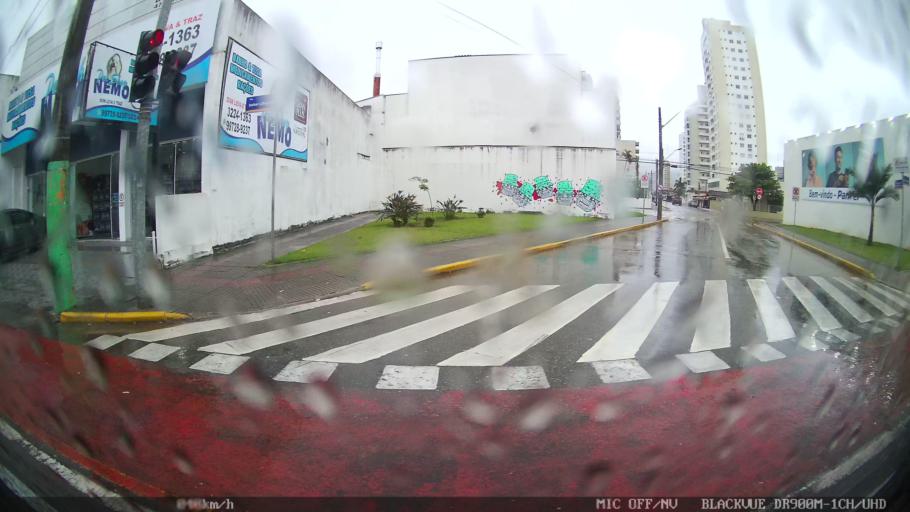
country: BR
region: Santa Catarina
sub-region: Itajai
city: Itajai
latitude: -26.9068
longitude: -48.6729
